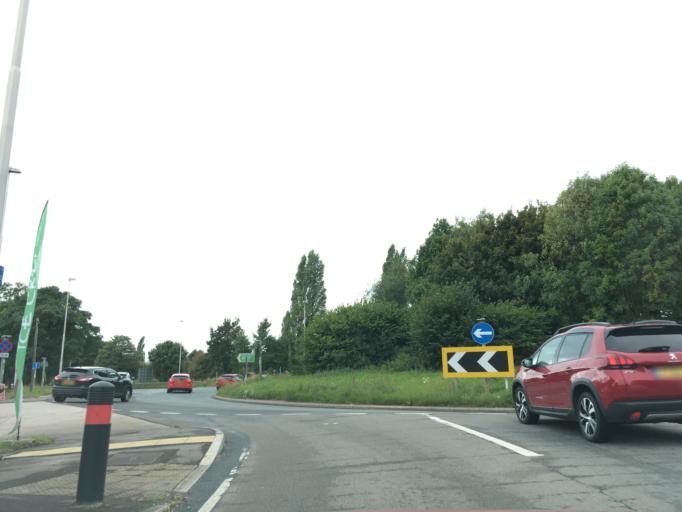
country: GB
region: England
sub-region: Herefordshire
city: Walford
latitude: 51.9160
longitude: -2.6003
